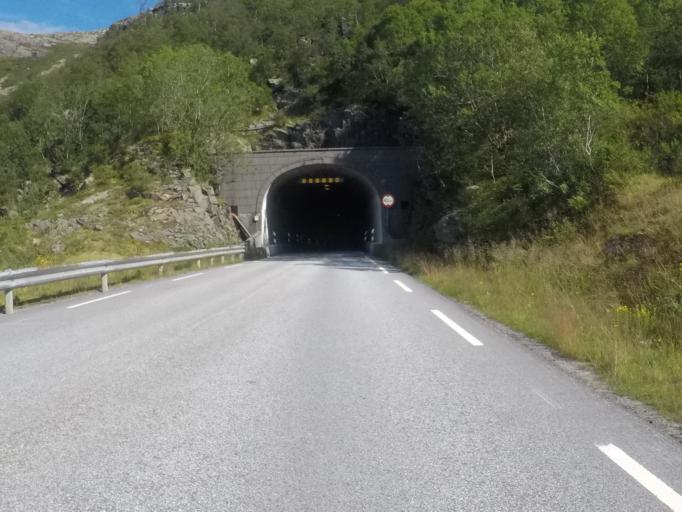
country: NO
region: Sogn og Fjordane
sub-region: Bremanger
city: Svelgen
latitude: 61.6673
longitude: 5.1950
